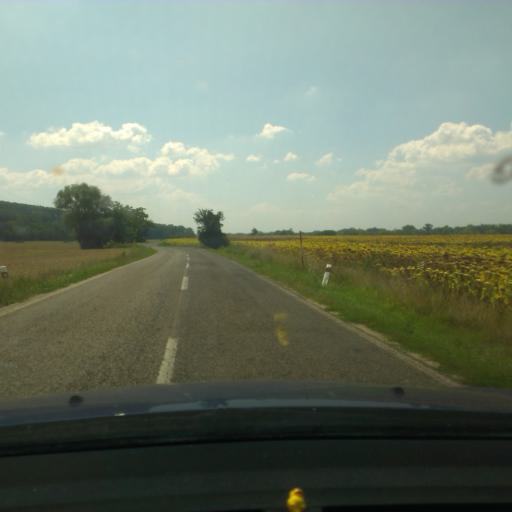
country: SK
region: Trnavsky
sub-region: Okres Trnava
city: Piestany
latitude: 48.5261
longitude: 17.8318
